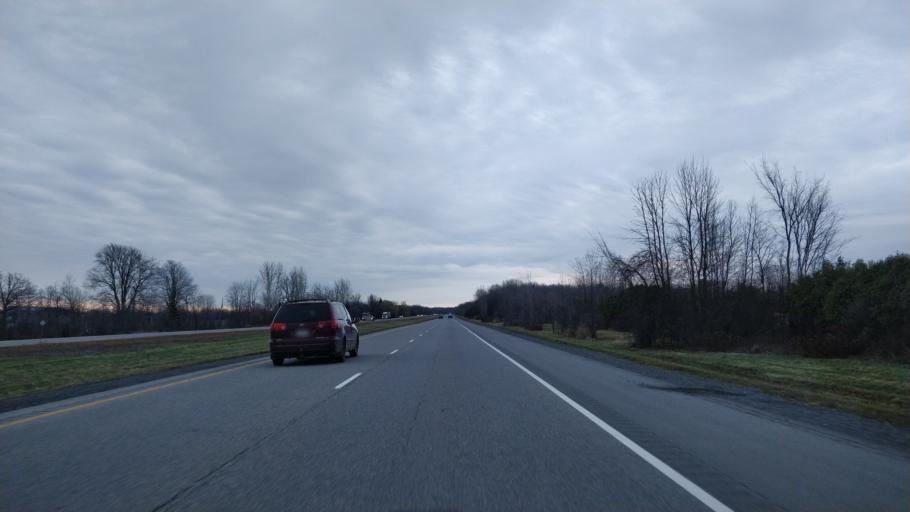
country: CA
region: Ontario
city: Bells Corners
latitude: 45.1773
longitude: -75.7065
